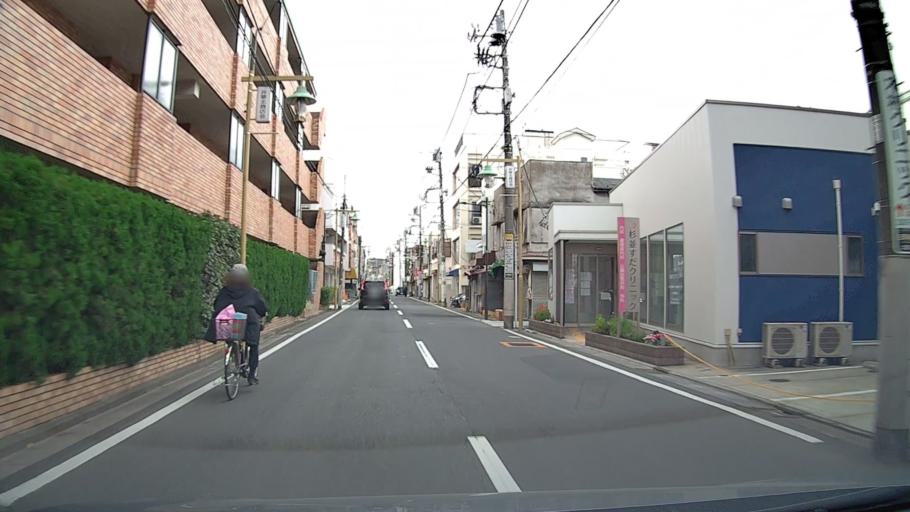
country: JP
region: Saitama
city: Wako
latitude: 35.7248
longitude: 139.6231
